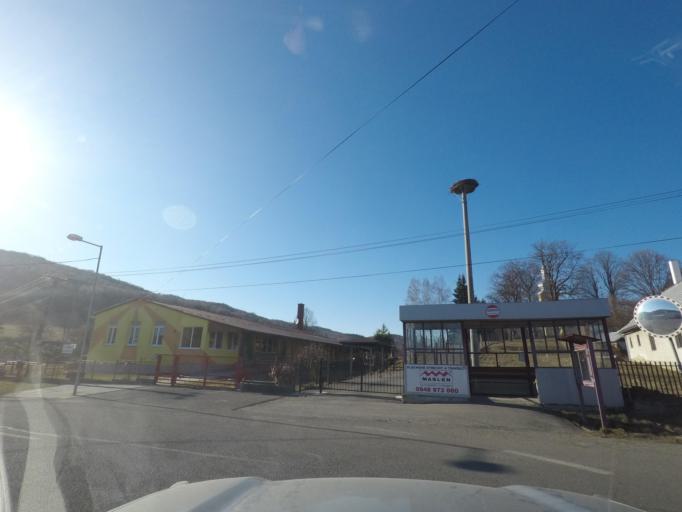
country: SK
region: Presovsky
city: Medzilaborce
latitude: 49.1917
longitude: 22.0056
